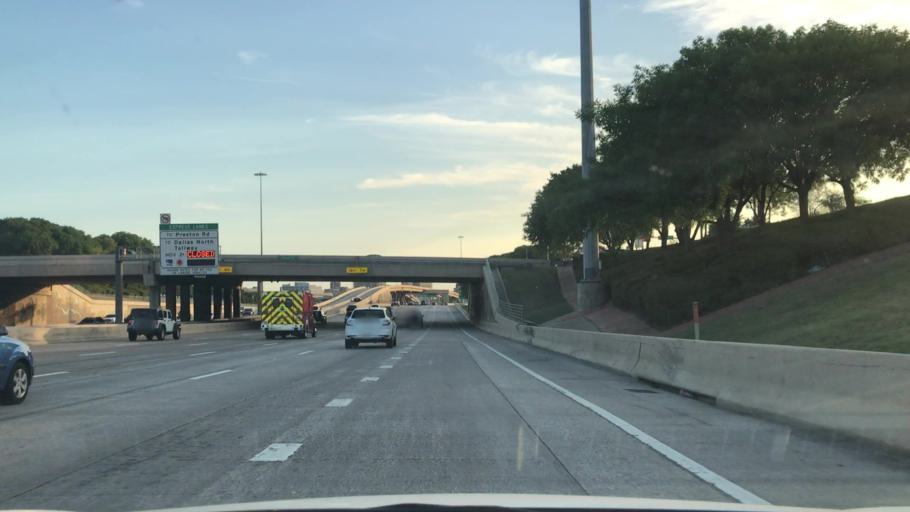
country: US
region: Texas
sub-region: Dallas County
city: Richardson
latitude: 32.9356
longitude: -96.7518
